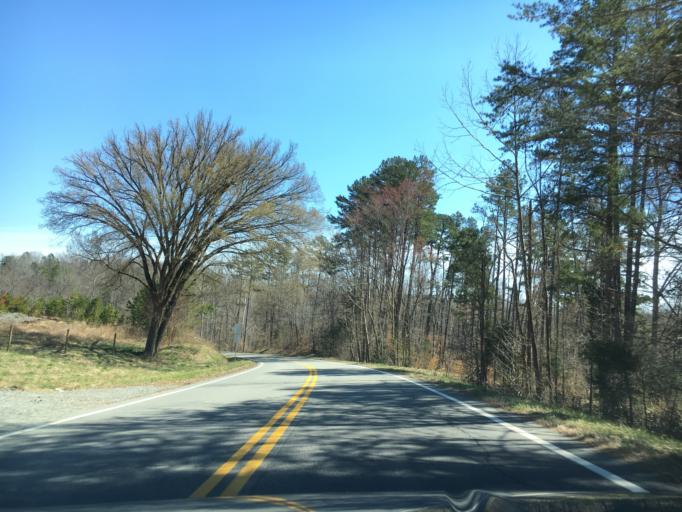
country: US
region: Virginia
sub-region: Halifax County
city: Halifax
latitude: 36.7601
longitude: -78.9092
